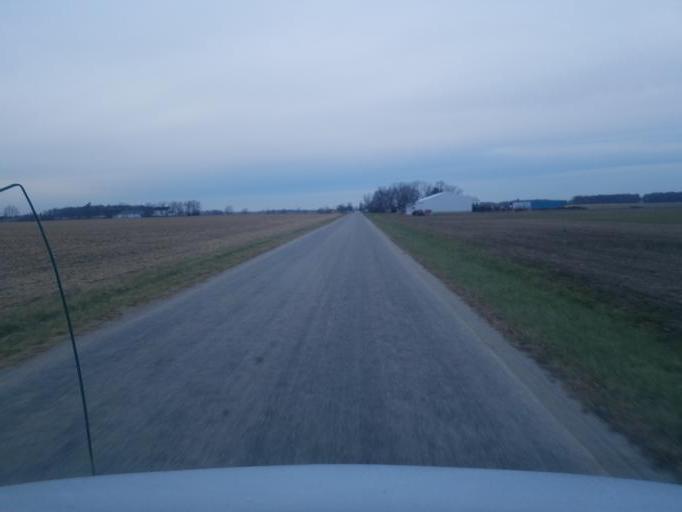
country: US
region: Indiana
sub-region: Adams County
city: Decatur
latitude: 40.7409
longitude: -84.8796
